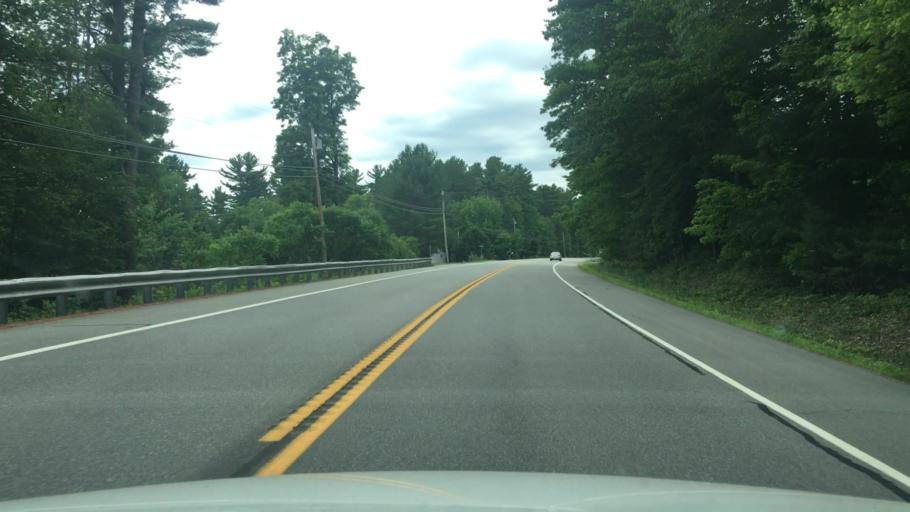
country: US
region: Maine
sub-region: Kennebec County
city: Windsor
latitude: 44.3521
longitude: -69.6460
